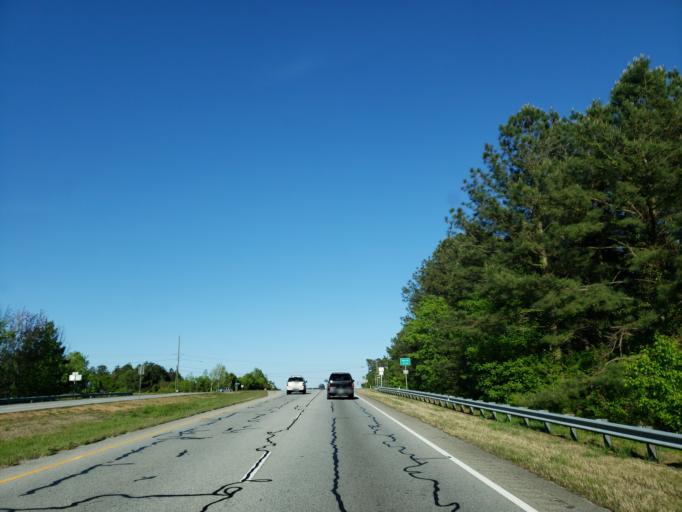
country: US
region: Georgia
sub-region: Paulding County
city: Dallas
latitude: 33.9134
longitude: -84.8902
